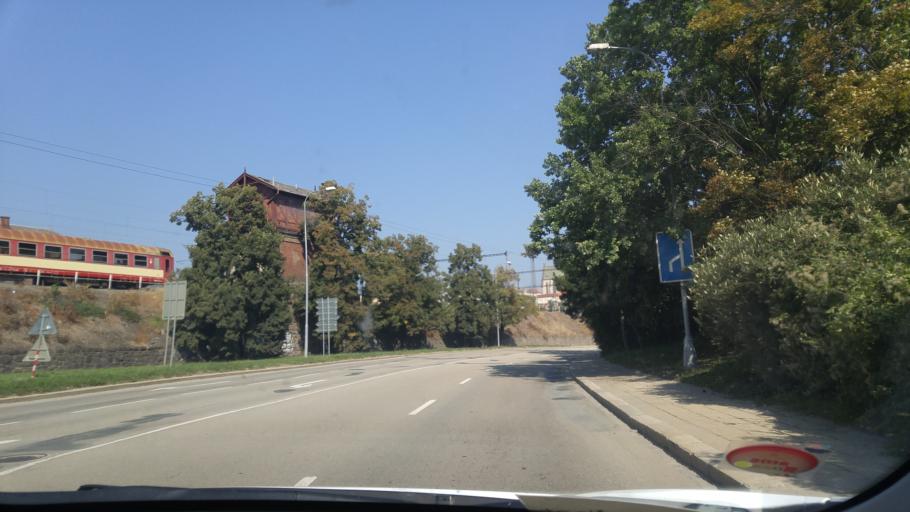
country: CZ
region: South Moravian
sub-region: Mesto Brno
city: Brno
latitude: 49.1842
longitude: 16.6083
